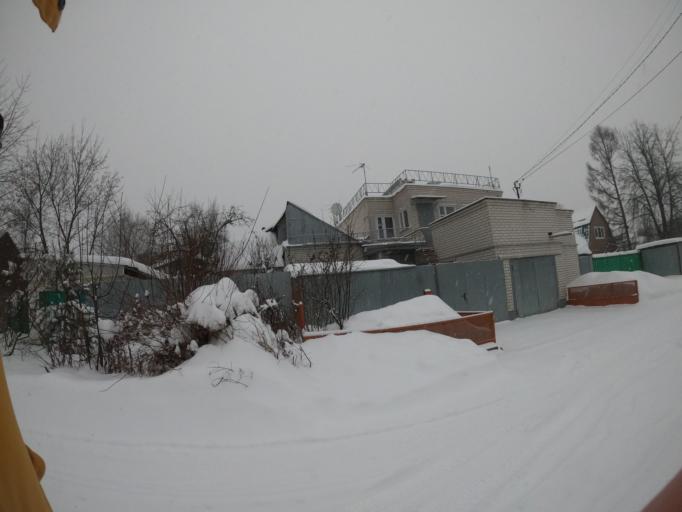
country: RU
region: Moskovskaya
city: Kupavna
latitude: 55.7499
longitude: 38.1392
